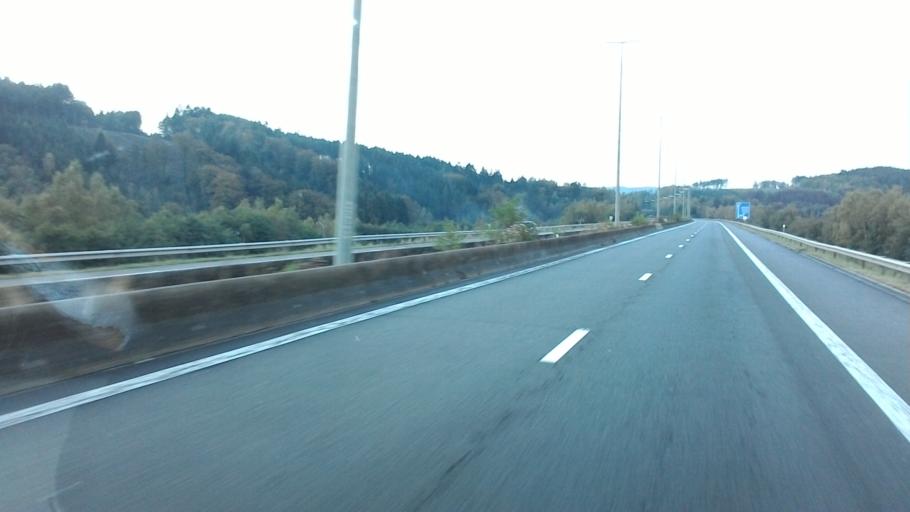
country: BE
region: Wallonia
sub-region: Province du Luxembourg
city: Manhay
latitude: 50.2941
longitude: 5.7255
